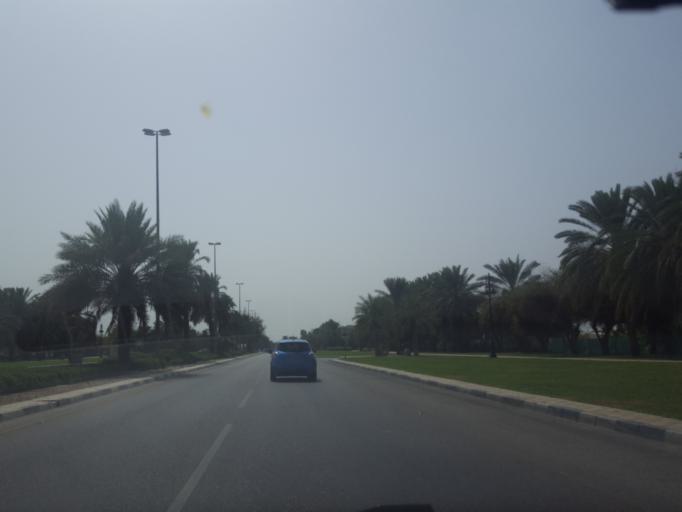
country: AE
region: Abu Dhabi
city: Al Ain
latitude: 24.2058
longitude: 55.7938
